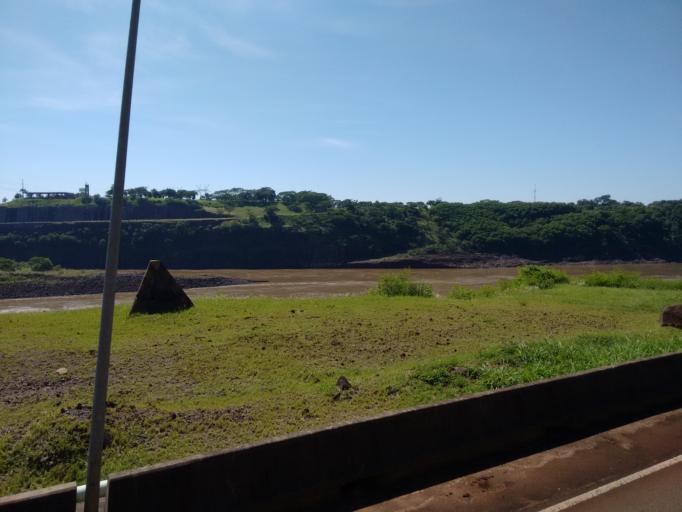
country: PY
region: Alto Parana
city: Ciudad del Este
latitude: -25.4117
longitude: -54.5934
